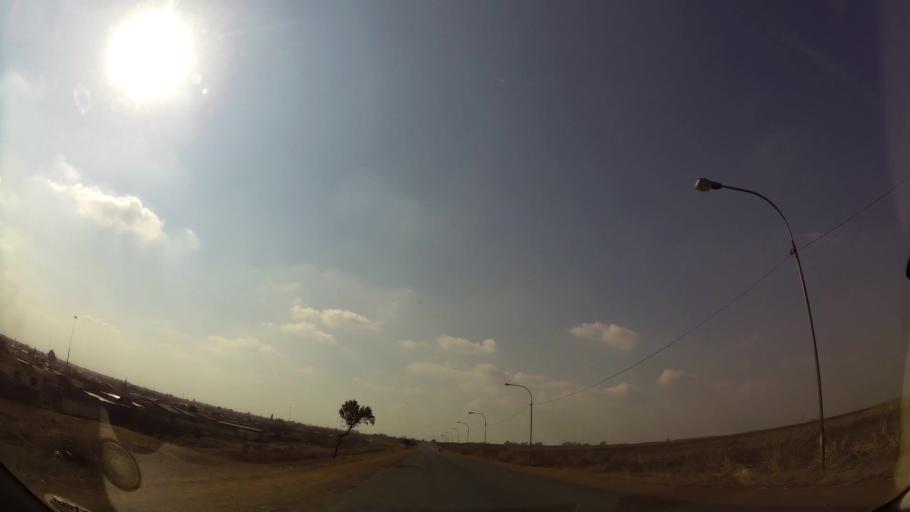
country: ZA
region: Gauteng
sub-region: Ekurhuleni Metropolitan Municipality
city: Springs
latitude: -26.1347
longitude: 28.4736
